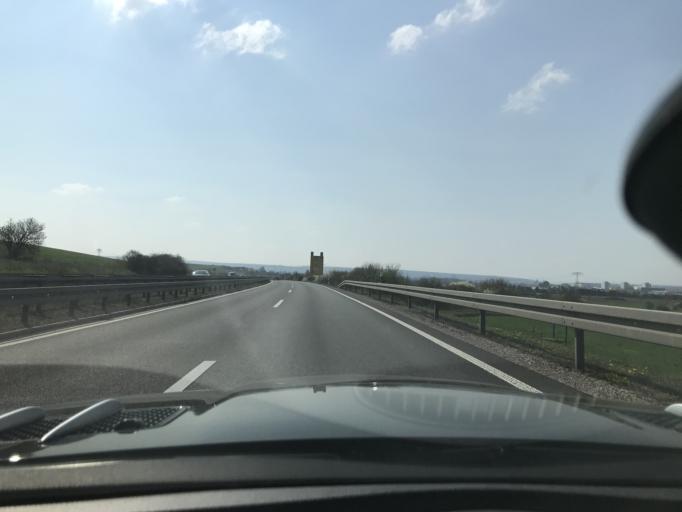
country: DE
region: Thuringia
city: Erfurt
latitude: 51.0211
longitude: 11.0574
